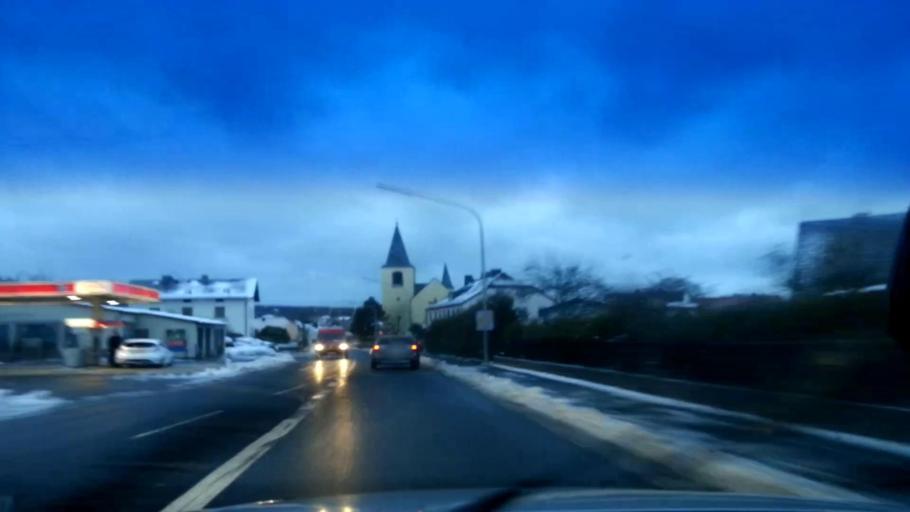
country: DE
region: Bavaria
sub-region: Upper Franconia
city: Kirchenlamitz
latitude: 50.1495
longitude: 11.9544
